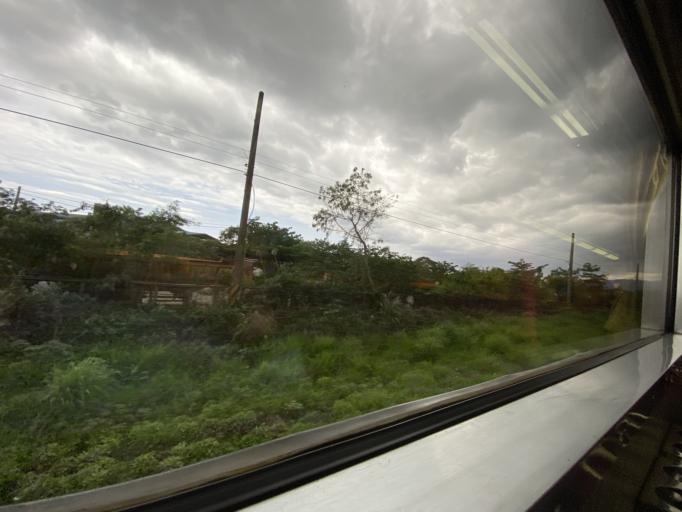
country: TW
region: Taiwan
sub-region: Taitung
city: Taitung
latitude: 22.7701
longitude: 121.1012
